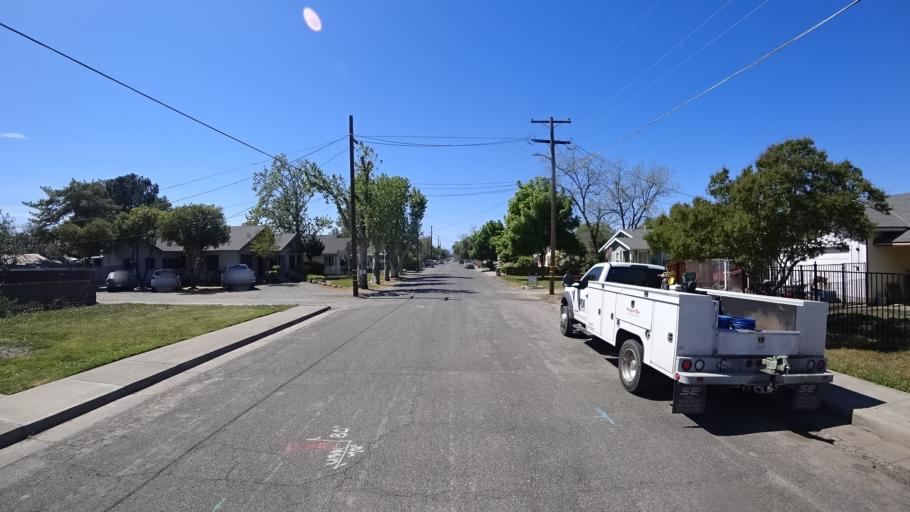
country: US
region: California
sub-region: Glenn County
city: Orland
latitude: 39.7462
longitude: -122.1844
